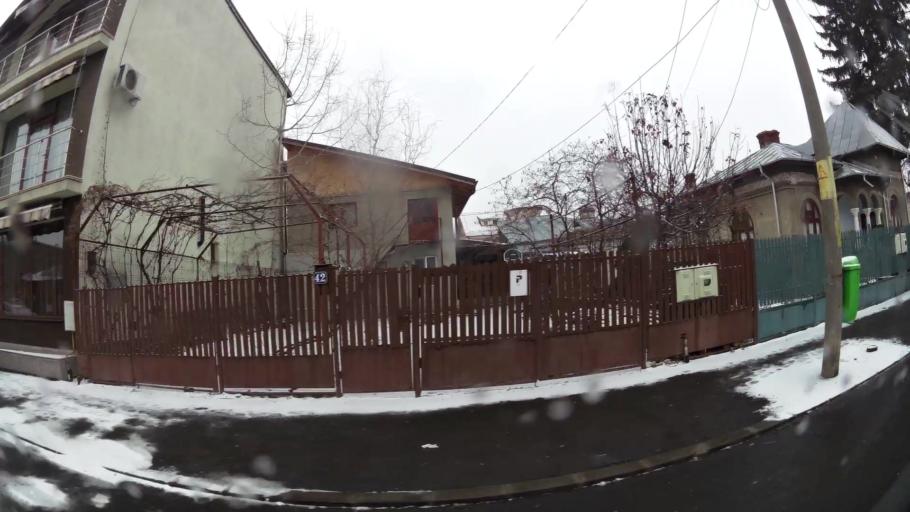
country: RO
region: Dambovita
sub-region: Municipiul Targoviste
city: Targoviste
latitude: 44.9246
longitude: 25.4527
